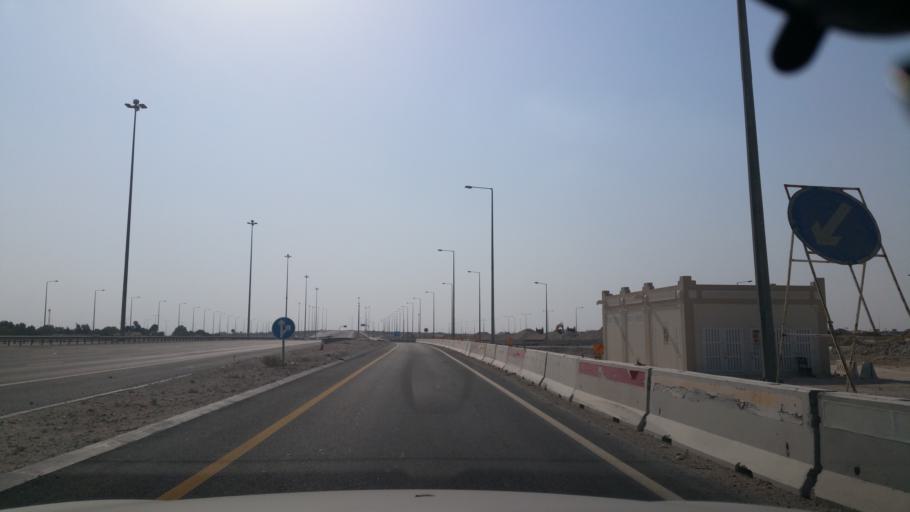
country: QA
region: Baladiyat Umm Salal
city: Umm Salal `Ali
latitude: 25.4514
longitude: 51.4211
